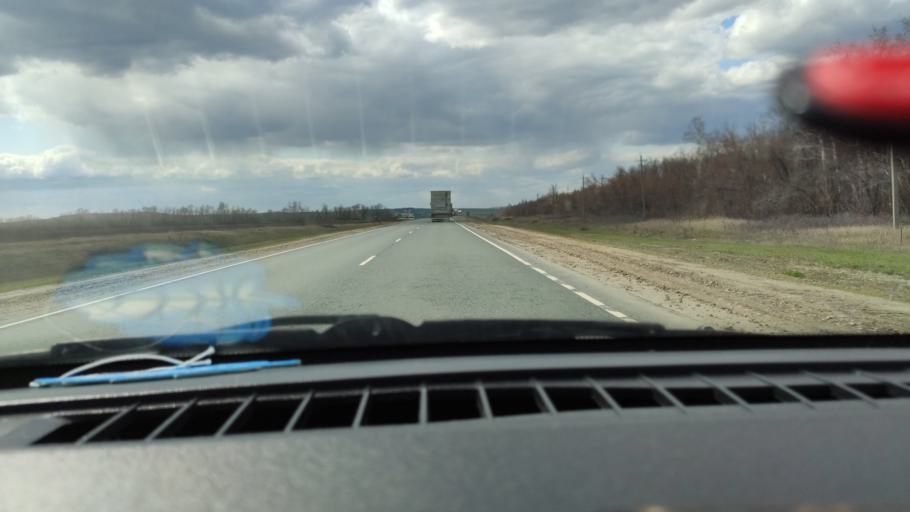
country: RU
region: Saratov
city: Alekseyevka
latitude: 52.2647
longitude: 47.9240
